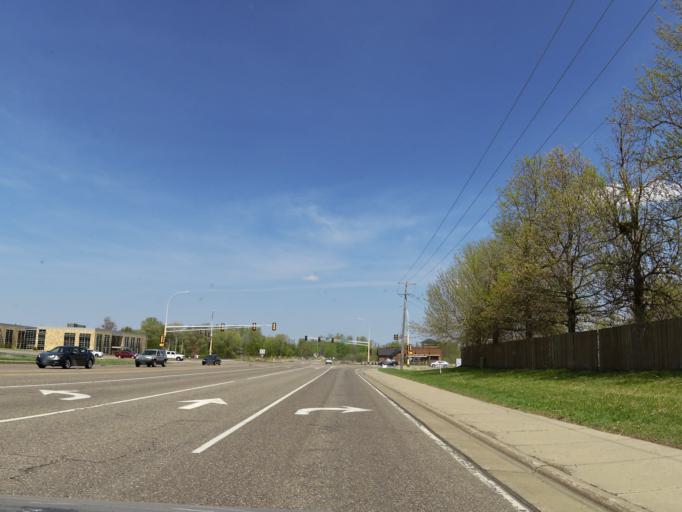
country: US
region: Minnesota
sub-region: Scott County
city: Savage
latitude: 44.7637
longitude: -93.3590
